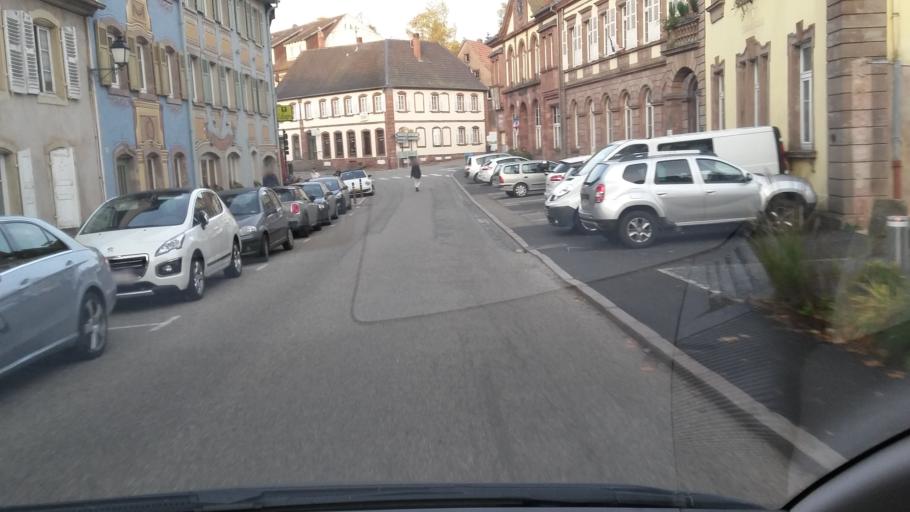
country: FR
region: Alsace
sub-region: Departement du Bas-Rhin
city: Neuwiller-les-Saverne
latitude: 48.8574
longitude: 7.3200
